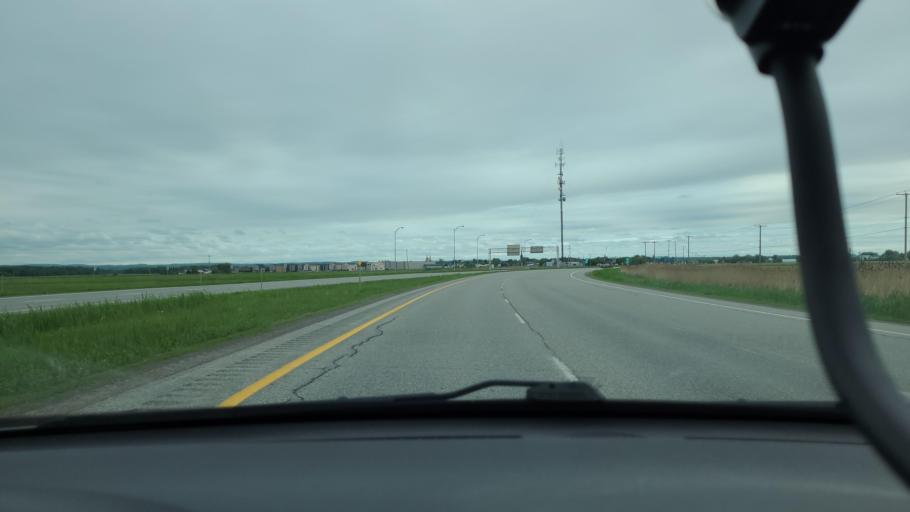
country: CA
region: Quebec
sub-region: Lanaudiere
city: Sainte-Julienne
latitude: 45.8851
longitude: -73.6606
